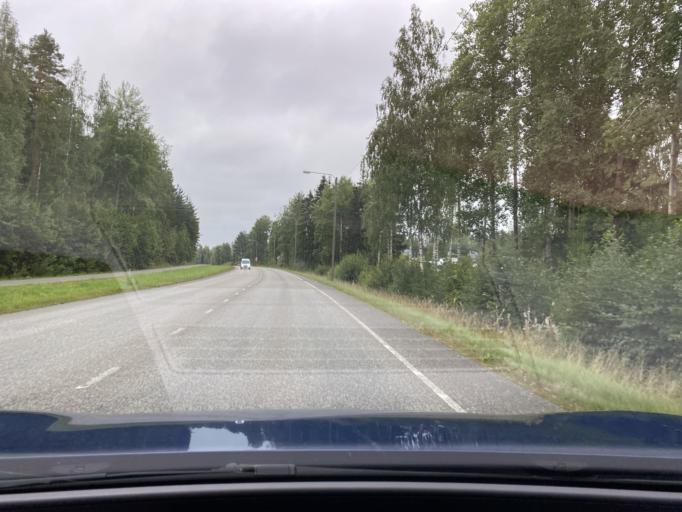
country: FI
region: Kymenlaakso
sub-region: Kouvola
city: Kouvola
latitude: 60.8979
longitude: 26.6049
